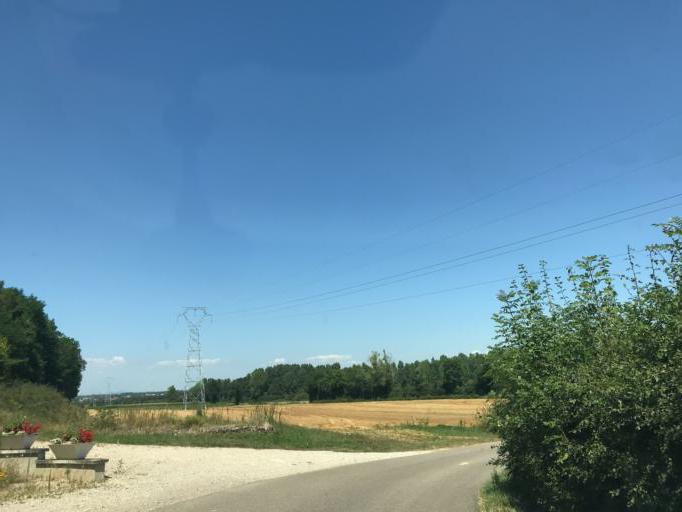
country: FR
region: Rhone-Alpes
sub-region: Departement de l'Ain
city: Tramoyes
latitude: 45.8813
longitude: 4.9624
